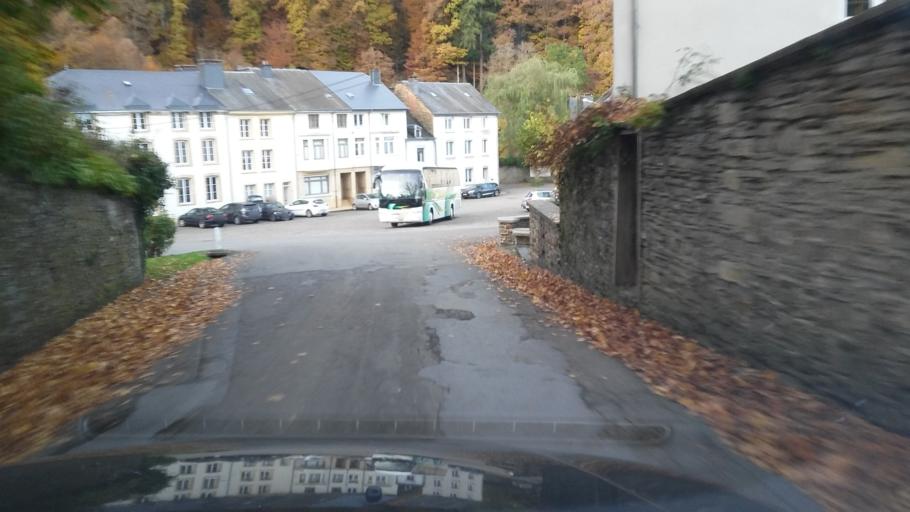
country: BE
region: Wallonia
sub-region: Province du Luxembourg
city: Bouillon
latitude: 49.7965
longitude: 5.0668
